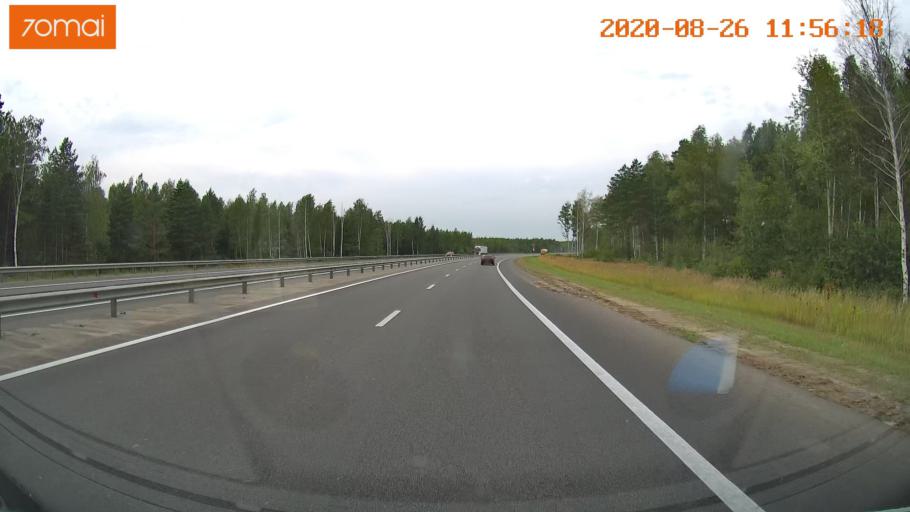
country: RU
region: Rjazan
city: Kiritsy
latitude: 54.2633
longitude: 40.3802
